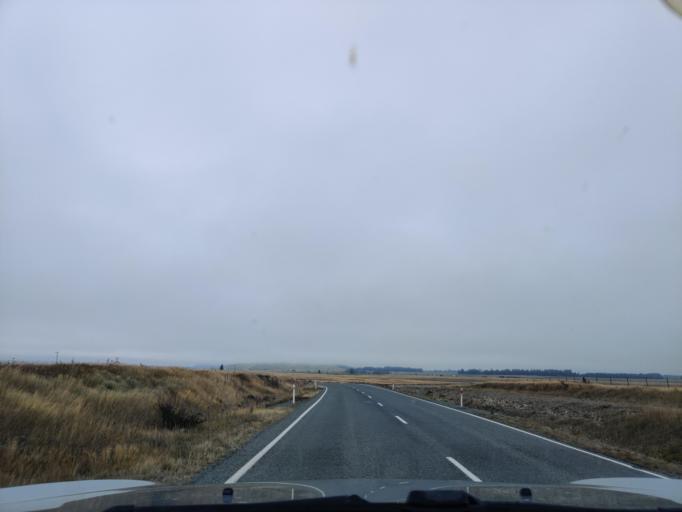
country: NZ
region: Canterbury
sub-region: Timaru District
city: Pleasant Point
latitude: -44.1555
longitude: 170.3360
